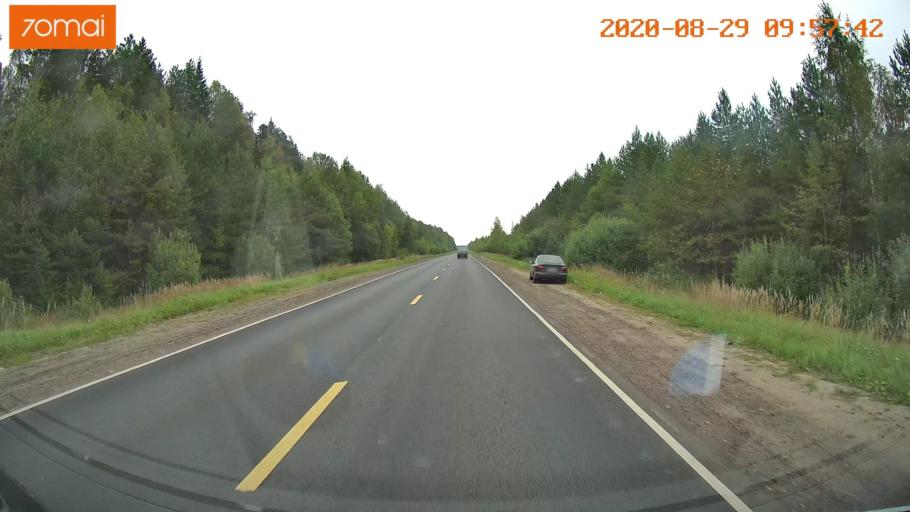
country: RU
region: Ivanovo
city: Zarechnyy
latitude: 57.4156
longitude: 42.3211
